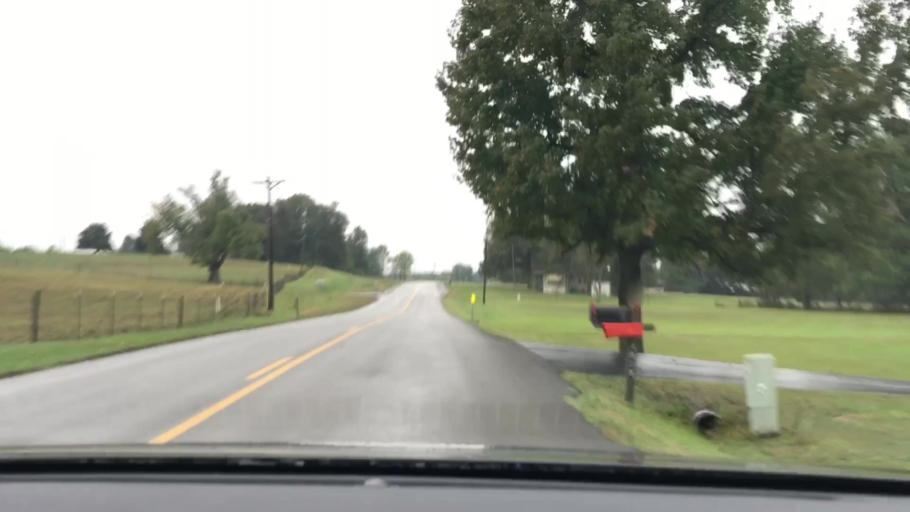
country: US
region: Kentucky
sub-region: Hopkins County
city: Madisonville
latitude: 37.3386
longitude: -87.4132
